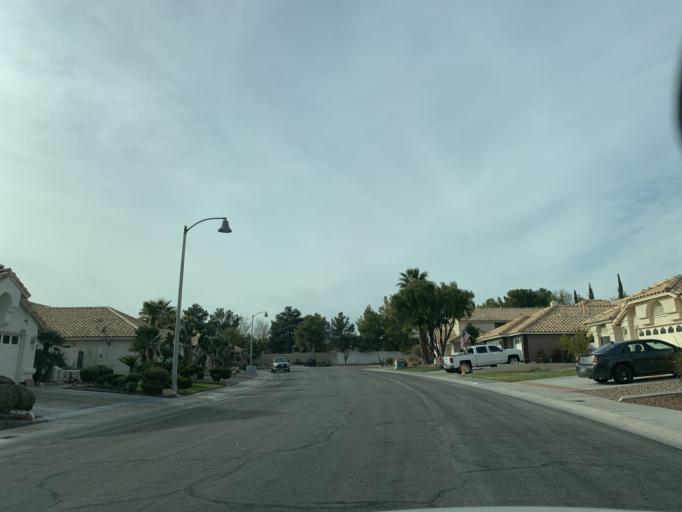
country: US
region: Nevada
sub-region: Clark County
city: Summerlin South
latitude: 36.1348
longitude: -115.3050
